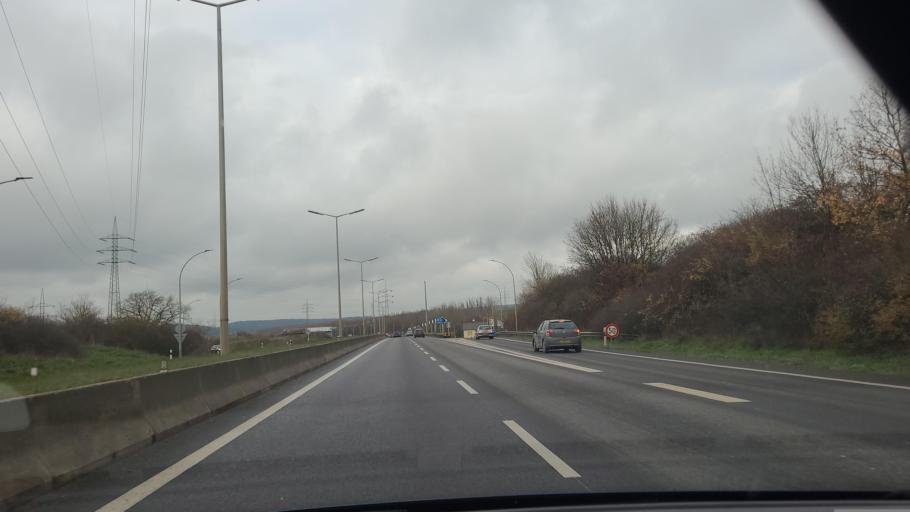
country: LU
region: Luxembourg
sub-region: Canton d'Esch-sur-Alzette
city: Sanem
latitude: 49.5418
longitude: 5.9205
